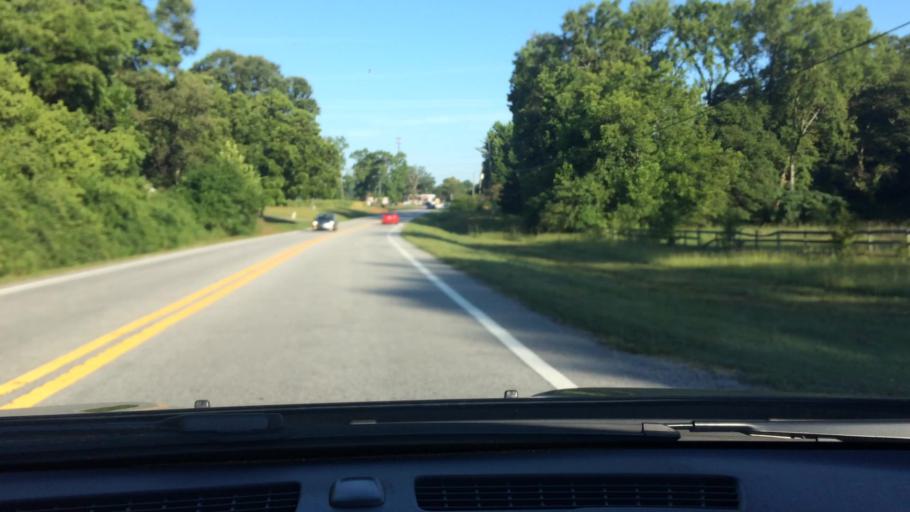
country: US
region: North Carolina
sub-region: Pitt County
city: Summerfield
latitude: 35.6311
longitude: -77.4407
